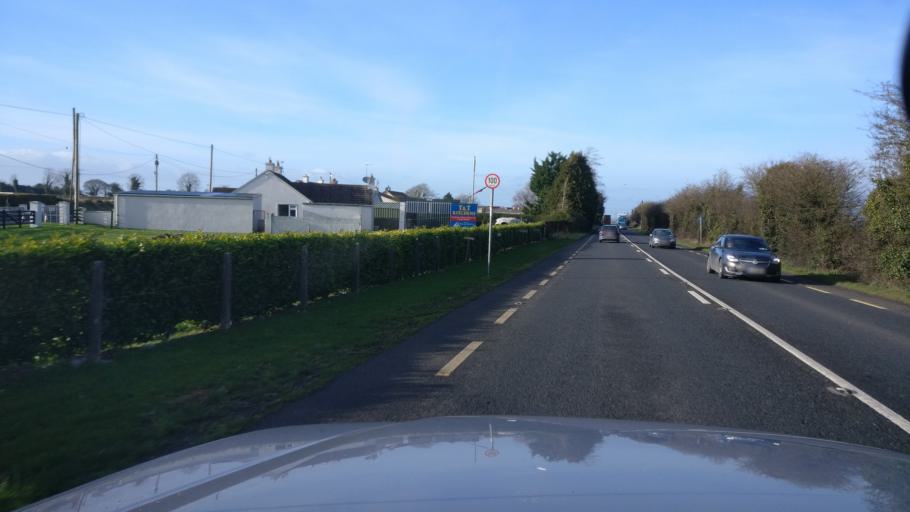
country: IE
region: Leinster
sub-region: Uibh Fhaili
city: Tullamore
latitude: 53.2063
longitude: -7.4351
